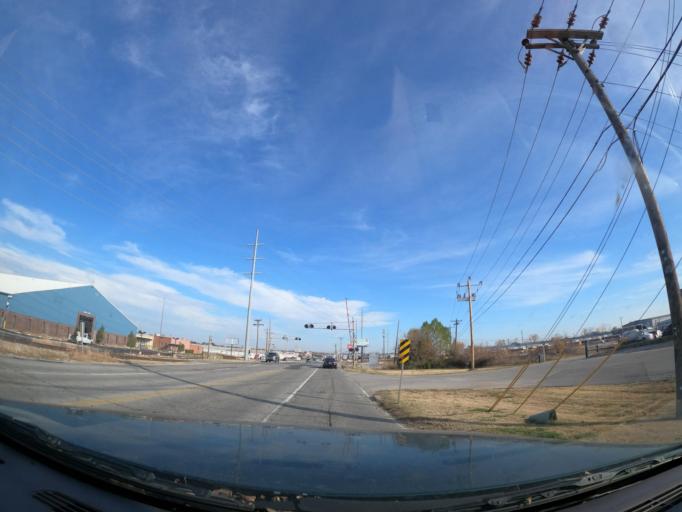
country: US
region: Oklahoma
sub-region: Tulsa County
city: Jenks
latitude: 36.1044
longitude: -95.8919
